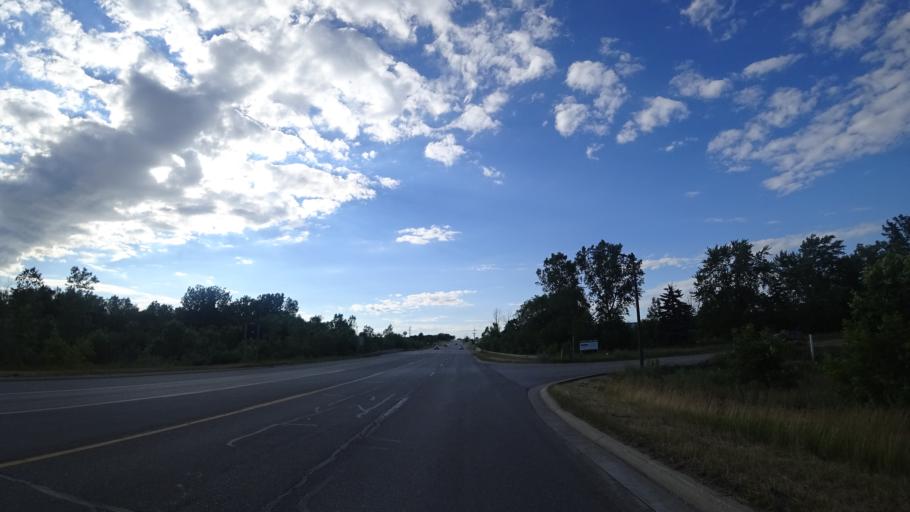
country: US
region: Michigan
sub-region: Ottawa County
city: Holland
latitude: 42.7463
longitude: -86.0743
